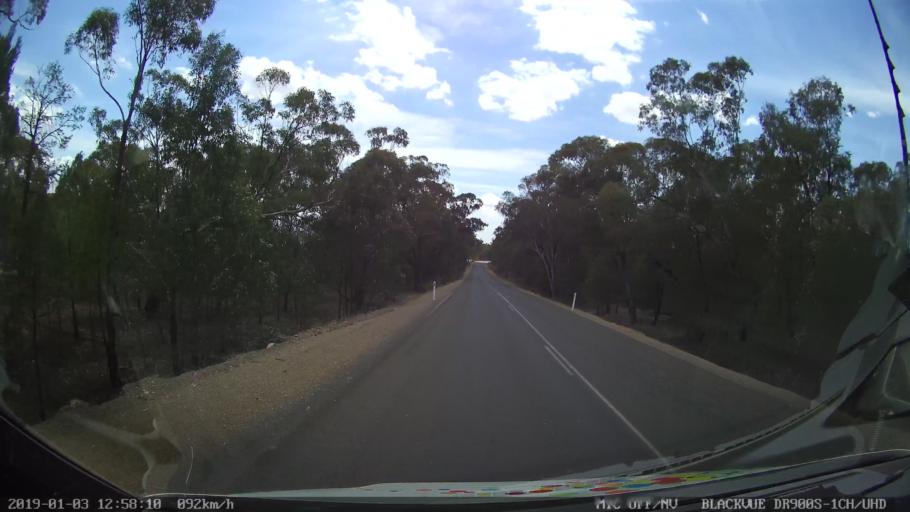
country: AU
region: New South Wales
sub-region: Cabonne
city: Canowindra
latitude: -33.6445
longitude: 148.3716
